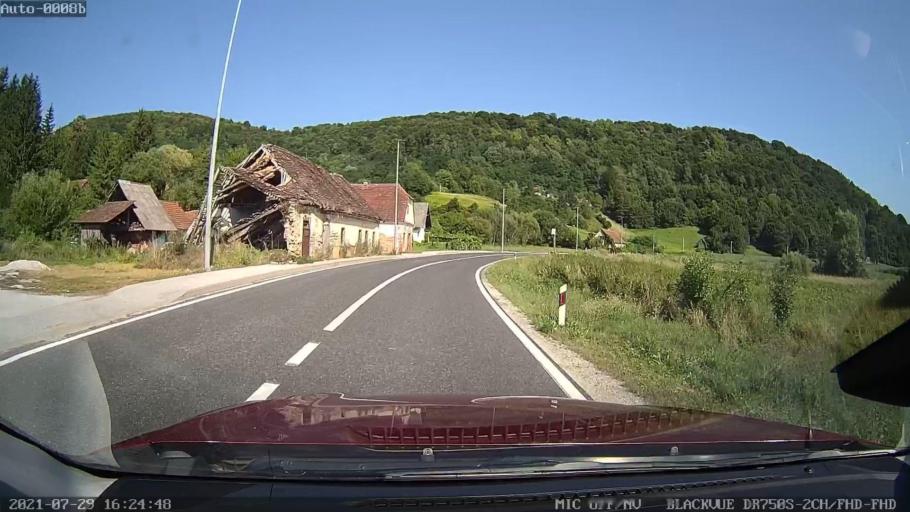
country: HR
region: Varazdinska
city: Lepoglava
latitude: 46.2314
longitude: 15.9887
